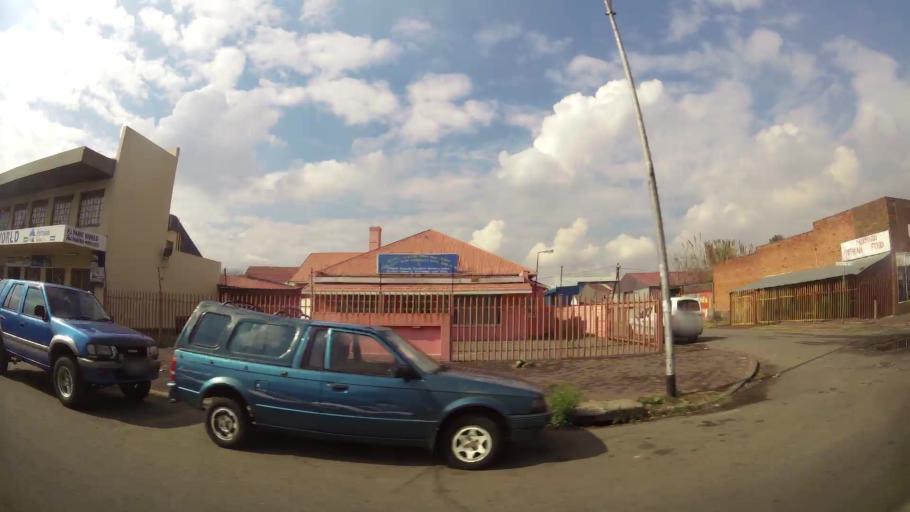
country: ZA
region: Gauteng
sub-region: Sedibeng District Municipality
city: Vereeniging
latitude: -26.6806
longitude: 27.9281
